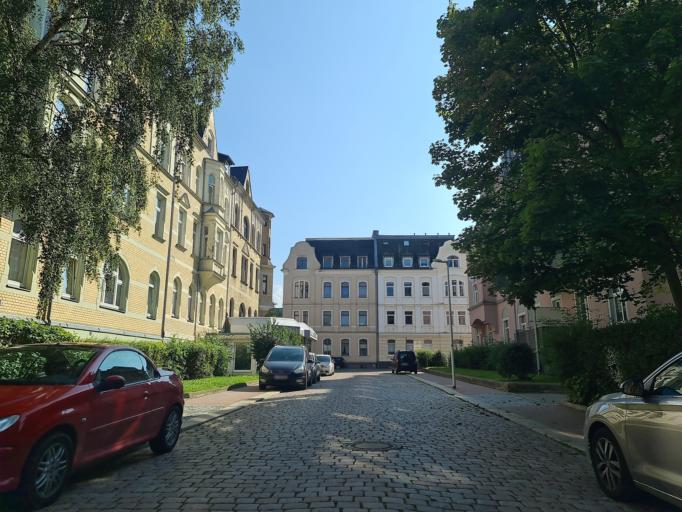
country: DE
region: Saxony
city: Plauen
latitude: 50.5129
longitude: 12.1476
